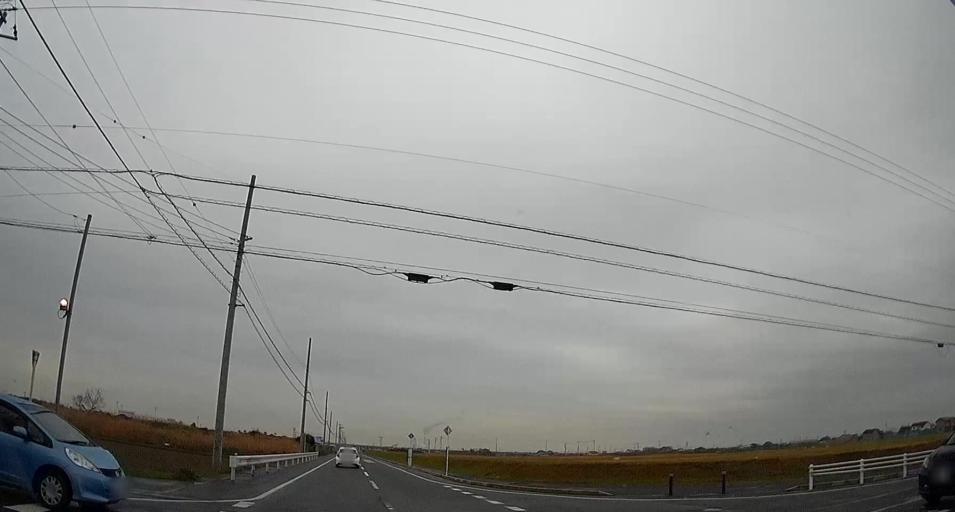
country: JP
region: Chiba
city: Kisarazu
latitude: 35.4277
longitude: 139.9137
